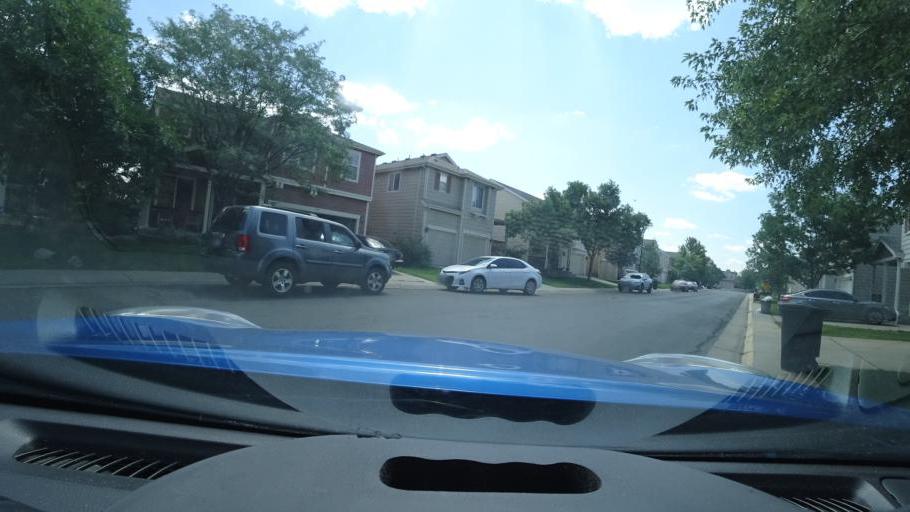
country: US
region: Colorado
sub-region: Arapahoe County
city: Glendale
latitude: 39.6961
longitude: -104.8803
